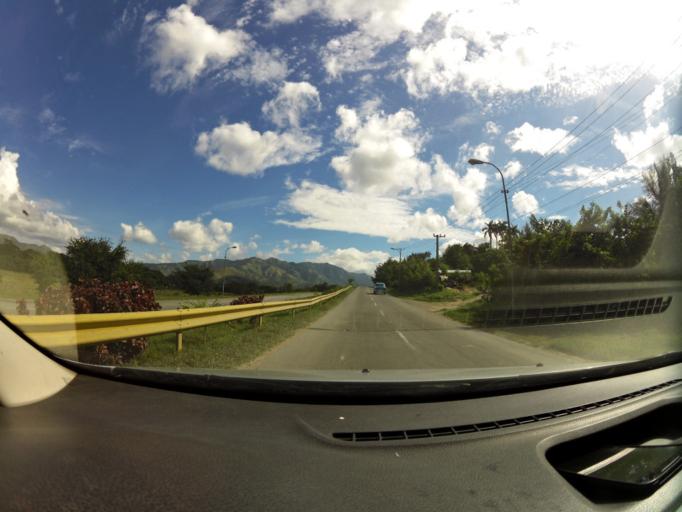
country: CU
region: Santiago de Cuba
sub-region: Municipio de Santiago de Cuba
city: Santiago de Cuba
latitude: 20.0141
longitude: -75.7784
